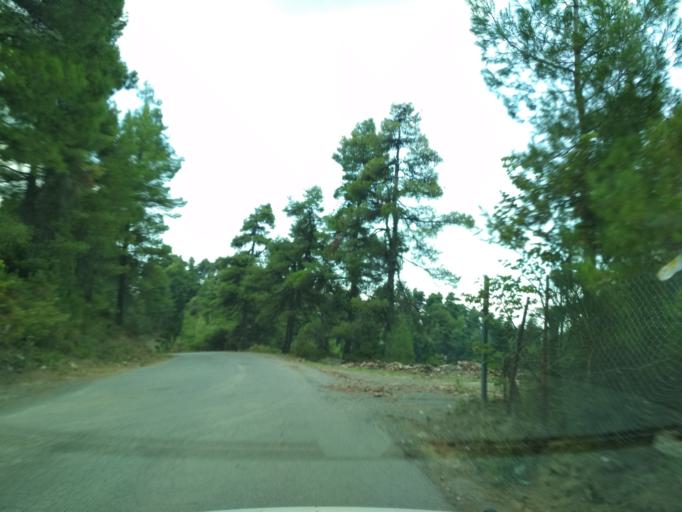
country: GR
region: Central Greece
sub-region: Nomos Evvoias
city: Roviai
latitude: 38.8539
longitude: 23.2889
